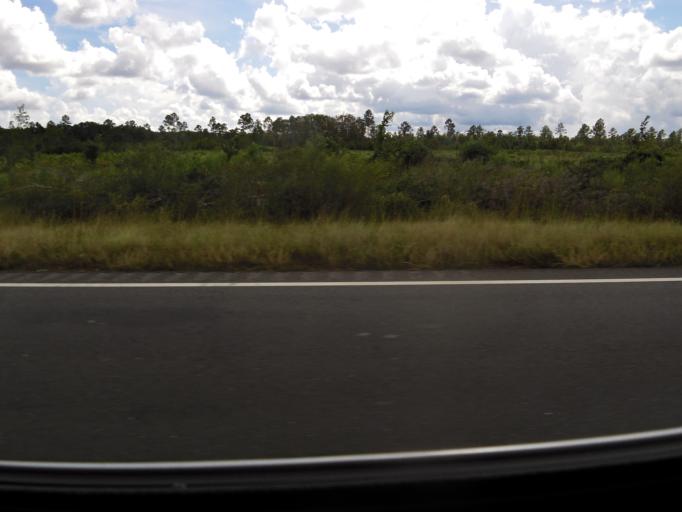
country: US
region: Georgia
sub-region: Glynn County
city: Dock Junction
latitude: 31.1835
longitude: -81.6415
